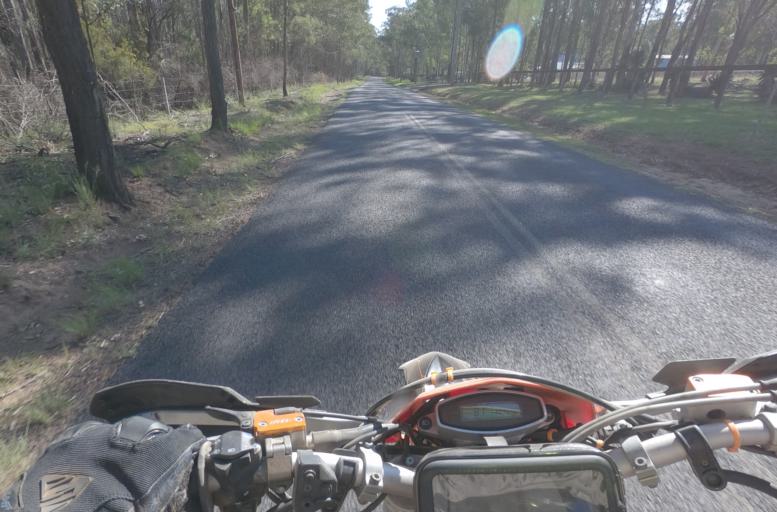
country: AU
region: New South Wales
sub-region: Hawkesbury
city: Scheyville
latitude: -33.5866
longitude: 150.9012
